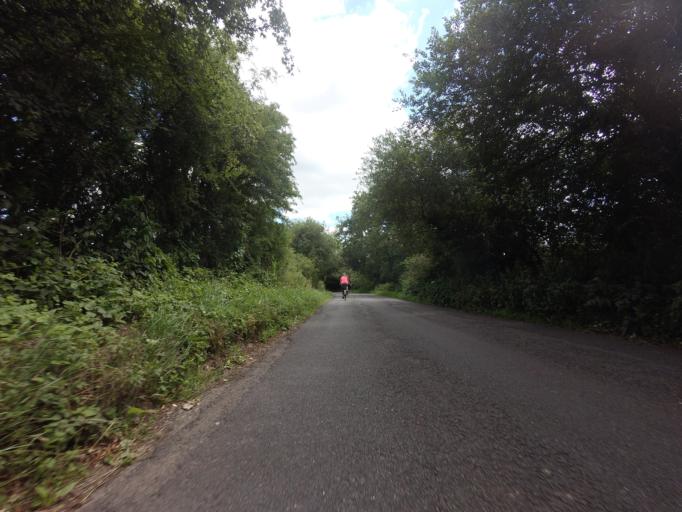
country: GB
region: England
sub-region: East Sussex
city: Hailsham
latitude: 50.8391
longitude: 0.1735
